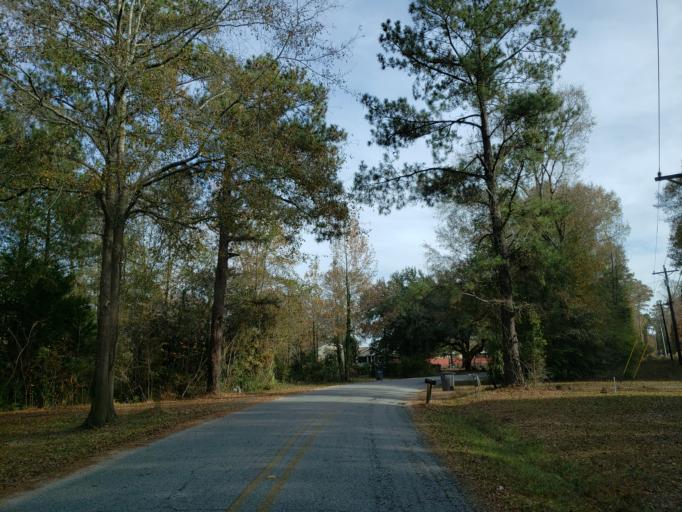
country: US
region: Mississippi
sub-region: Forrest County
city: Rawls Springs
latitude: 31.3779
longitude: -89.3690
